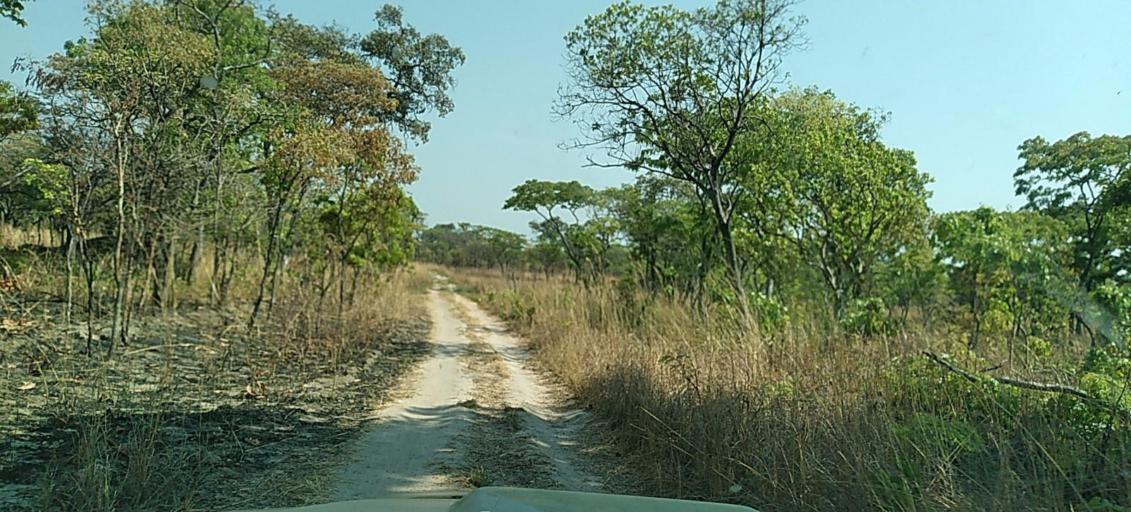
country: ZM
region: North-Western
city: Kalengwa
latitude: -13.3123
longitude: 24.8123
